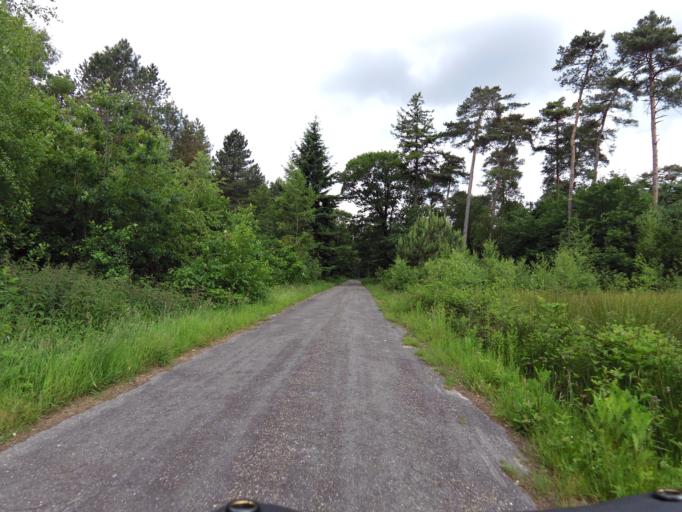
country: NL
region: North Brabant
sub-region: Gemeente Baarle-Nassau
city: Baarle-Nassau
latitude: 51.5054
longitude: 4.9032
